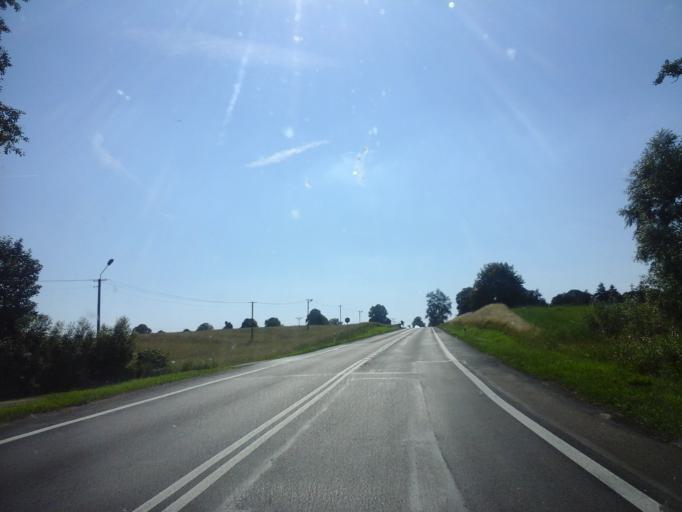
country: PL
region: West Pomeranian Voivodeship
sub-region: Powiat bialogardzki
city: Karlino
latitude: 53.9959
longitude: 15.7698
